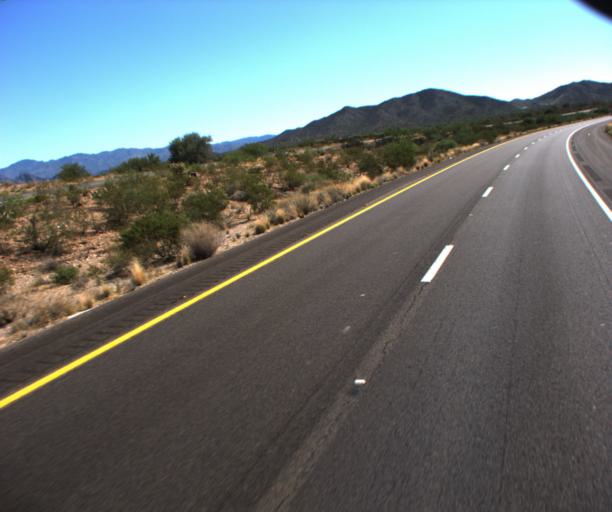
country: US
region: Arizona
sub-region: Pinal County
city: Gold Camp
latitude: 33.2629
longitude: -111.2747
